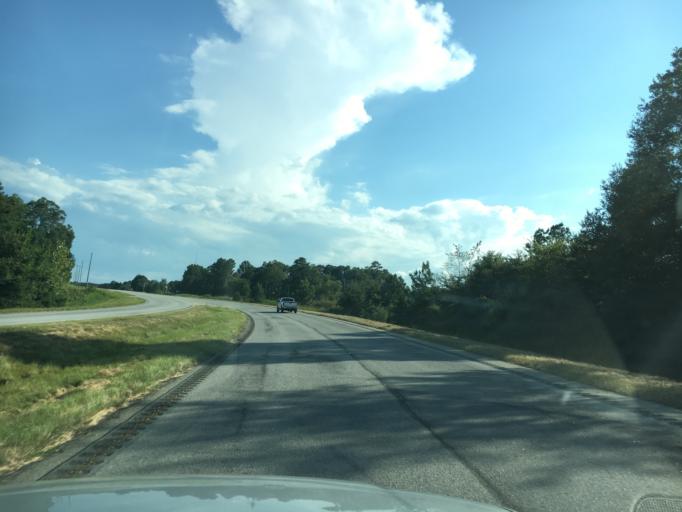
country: US
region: South Carolina
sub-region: Laurens County
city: Clinton
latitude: 34.3654
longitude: -81.9666
